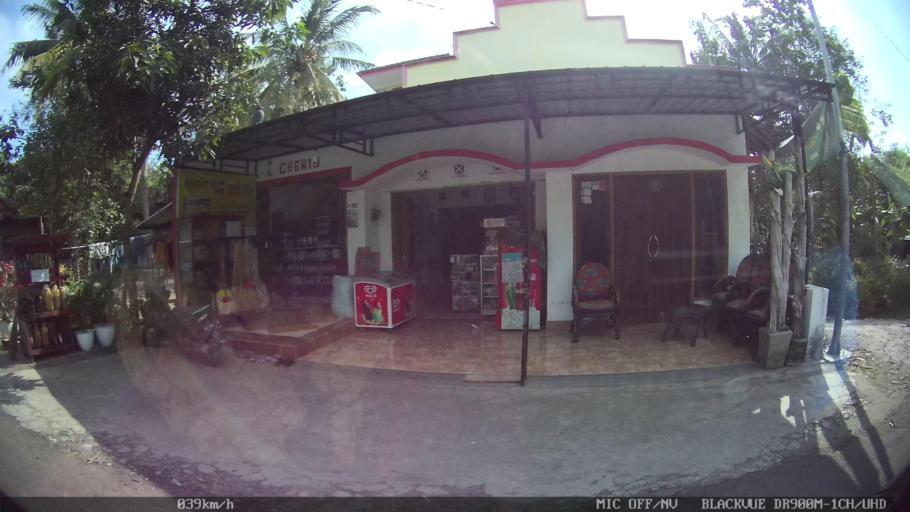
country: ID
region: Daerah Istimewa Yogyakarta
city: Kasihan
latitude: -7.8513
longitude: 110.3001
